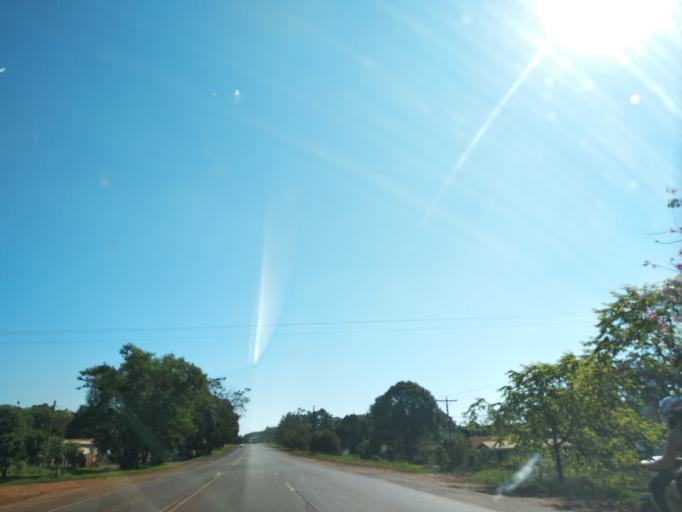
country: AR
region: Misiones
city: Garuhape
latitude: -26.8217
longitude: -54.9704
